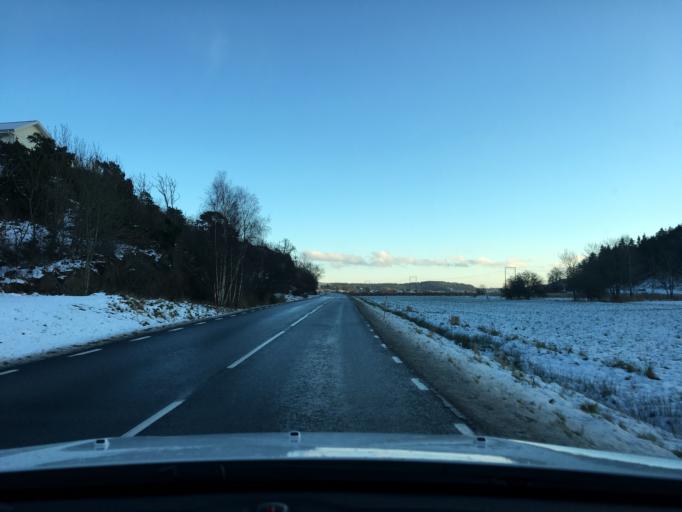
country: SE
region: Vaestra Goetaland
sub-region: Tjorns Kommun
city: Myggenas
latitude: 58.1238
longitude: 11.7283
